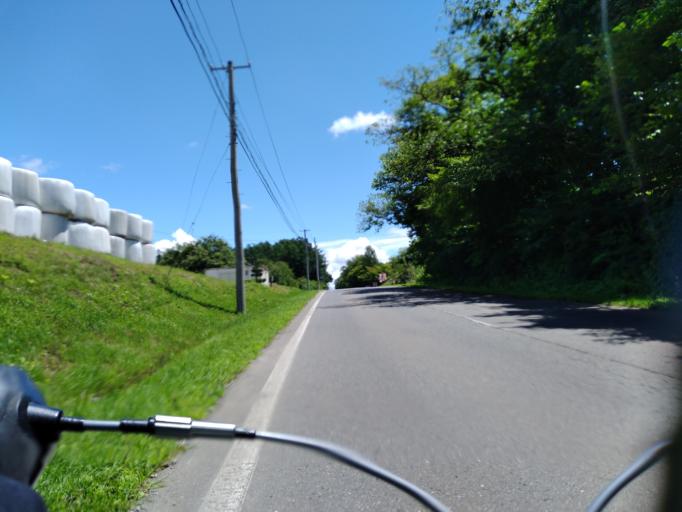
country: JP
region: Iwate
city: Shizukuishi
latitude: 39.7614
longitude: 140.9675
